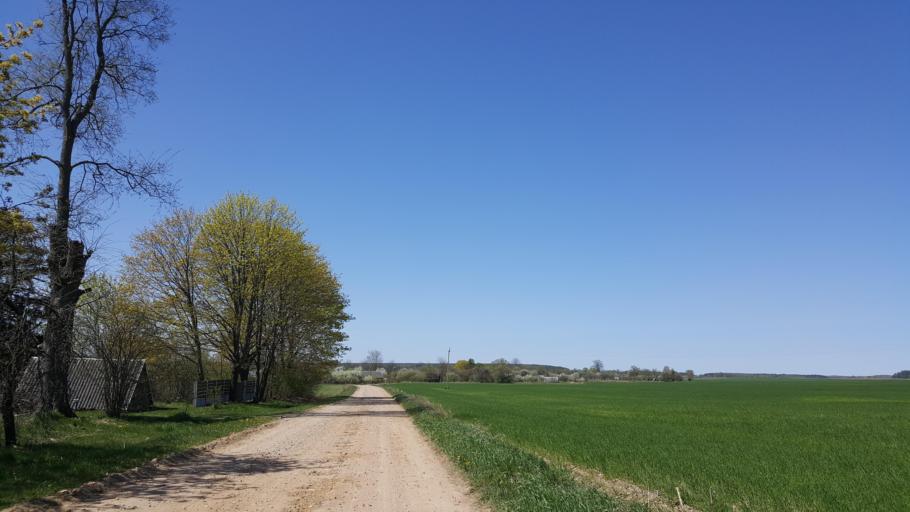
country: BY
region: Brest
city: Charnawchytsy
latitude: 52.3167
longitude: 23.7359
